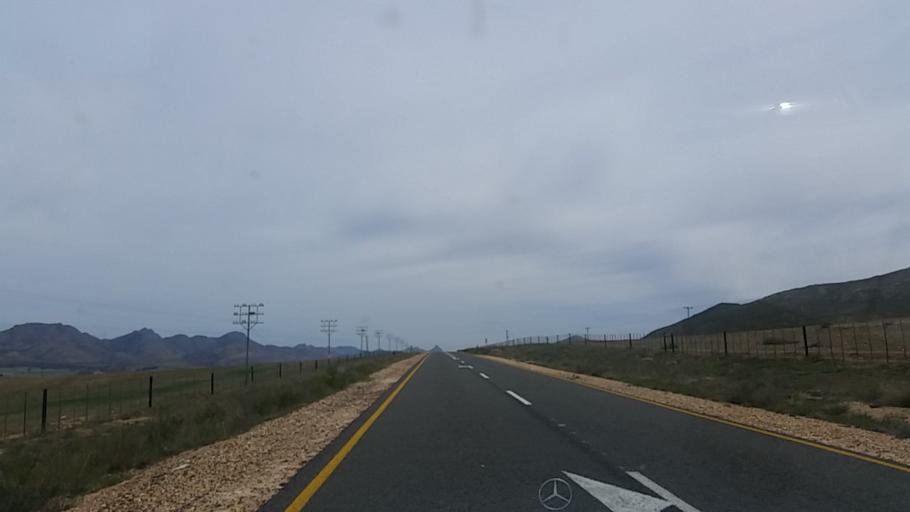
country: ZA
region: Western Cape
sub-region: Eden District Municipality
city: George
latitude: -33.7902
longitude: 22.6376
